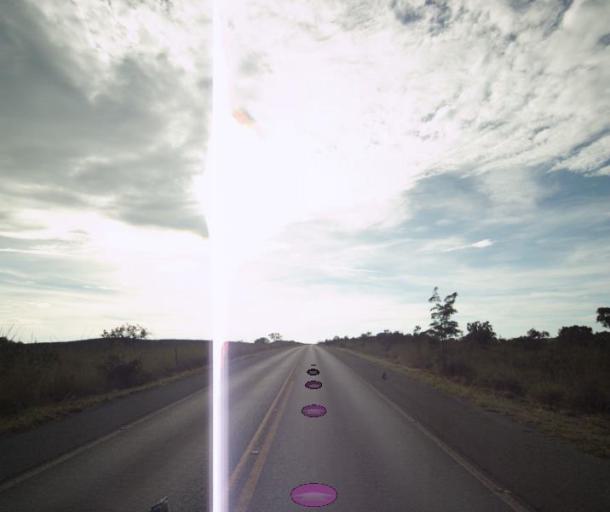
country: BR
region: Goias
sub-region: Pirenopolis
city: Pirenopolis
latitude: -15.7508
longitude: -48.6266
